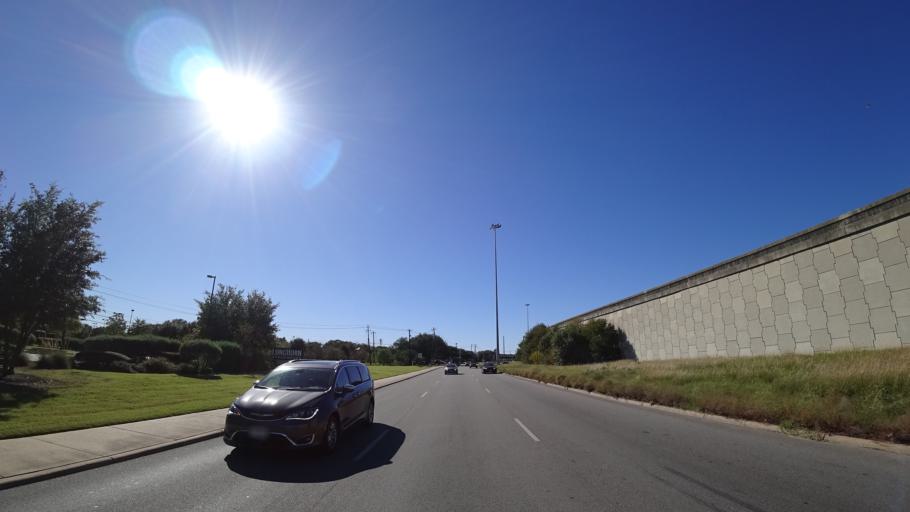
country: US
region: Texas
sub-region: Travis County
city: Rollingwood
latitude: 30.2327
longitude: -97.8166
